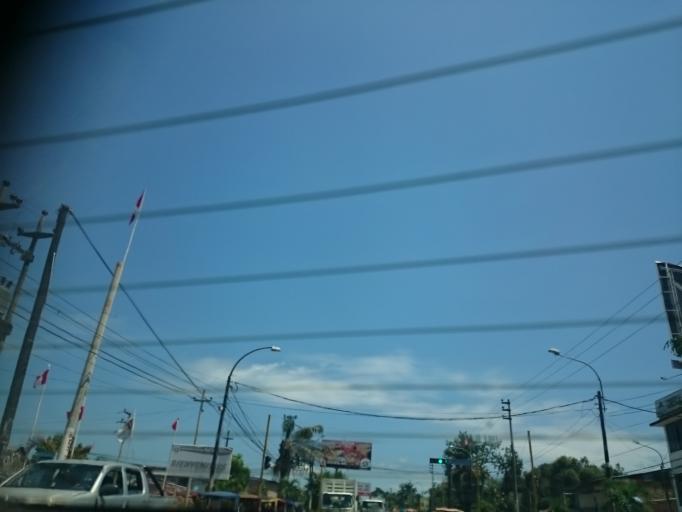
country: PE
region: Loreto
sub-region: Provincia de Maynas
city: Iquitos
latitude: -3.7700
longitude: -73.2802
